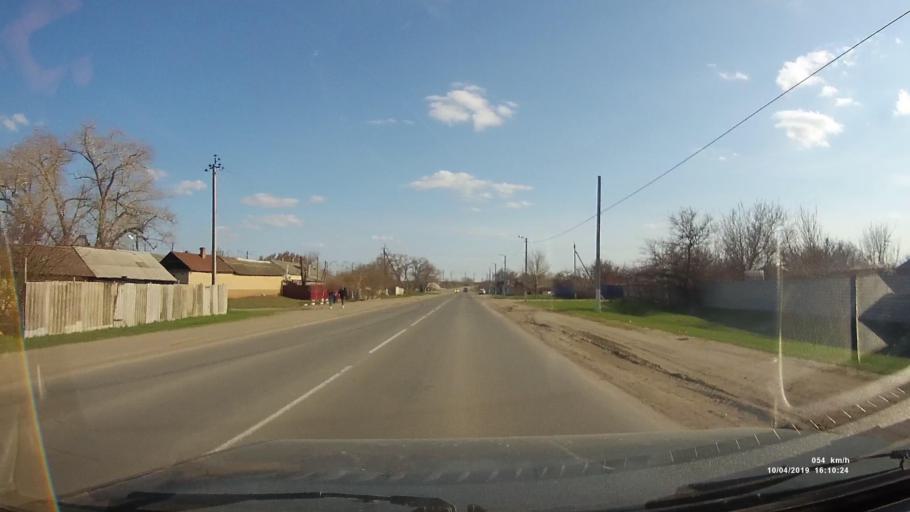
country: RU
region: Rostov
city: Staraya Stanitsa
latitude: 48.3525
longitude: 40.2695
